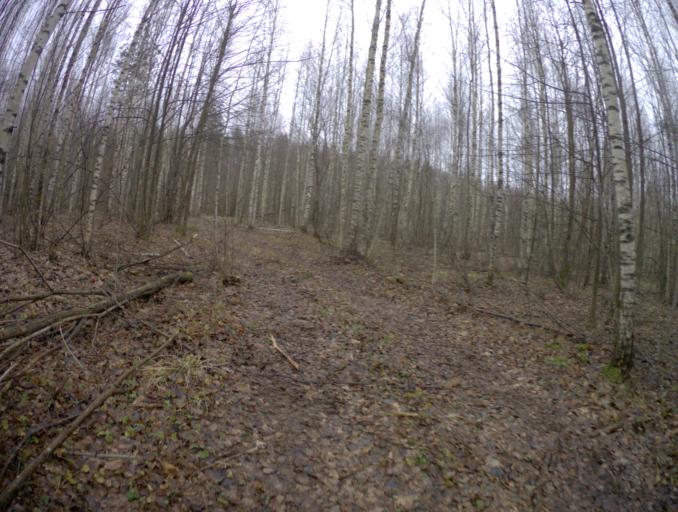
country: RU
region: Vladimir
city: Golovino
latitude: 56.0131
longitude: 40.5376
